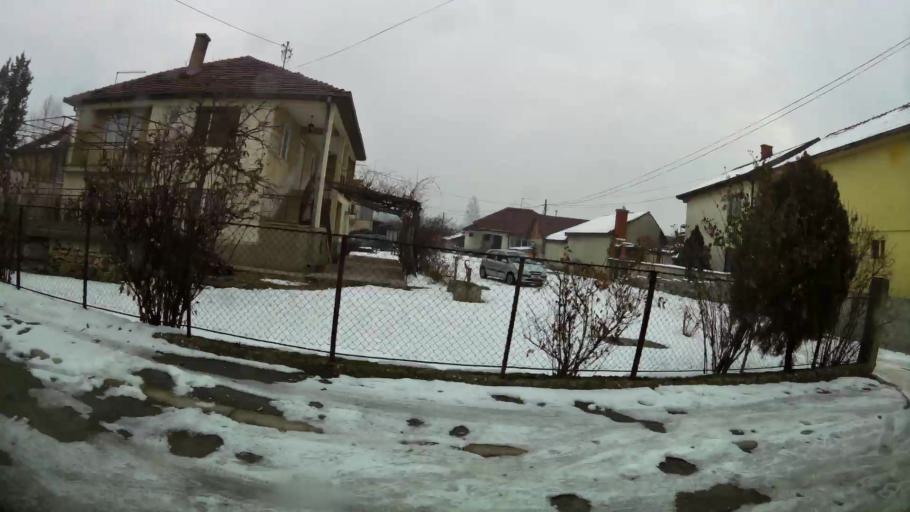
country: MK
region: Saraj
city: Saraj
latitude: 42.0296
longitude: 21.3545
